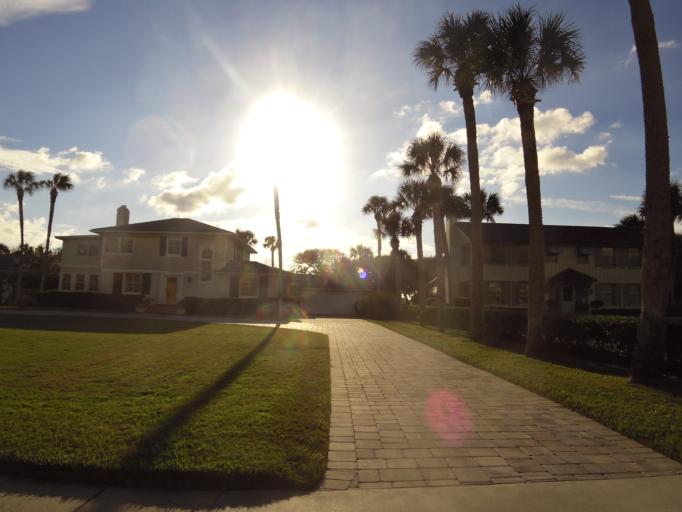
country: US
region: Florida
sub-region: Saint Johns County
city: Ponte Vedra Beach
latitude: 30.2350
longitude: -81.3768
